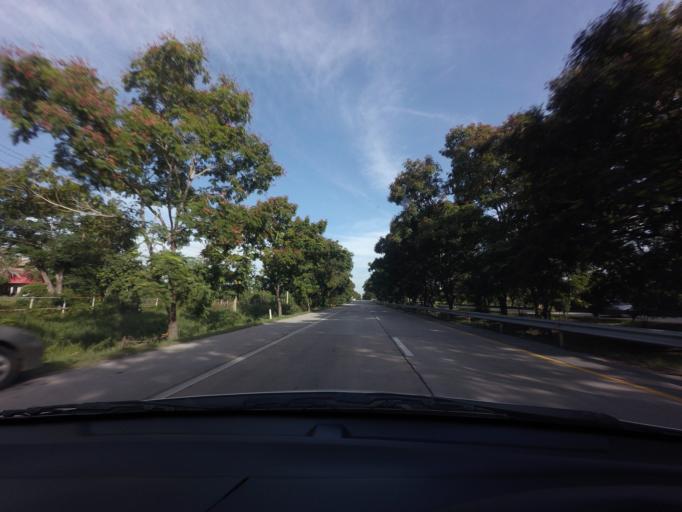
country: TH
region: Phra Nakhon Si Ayutthaya
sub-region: Amphoe Bang Sai
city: Bang Sai
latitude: 14.3107
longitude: 100.2264
